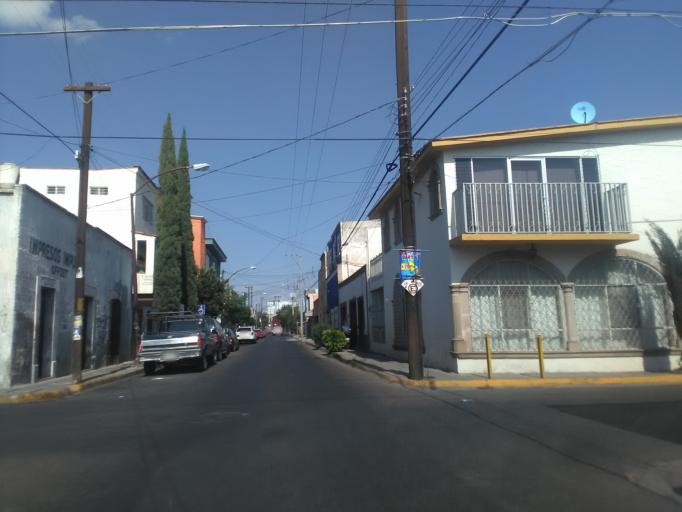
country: MX
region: Durango
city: Victoria de Durango
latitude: 24.0280
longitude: -104.6627
